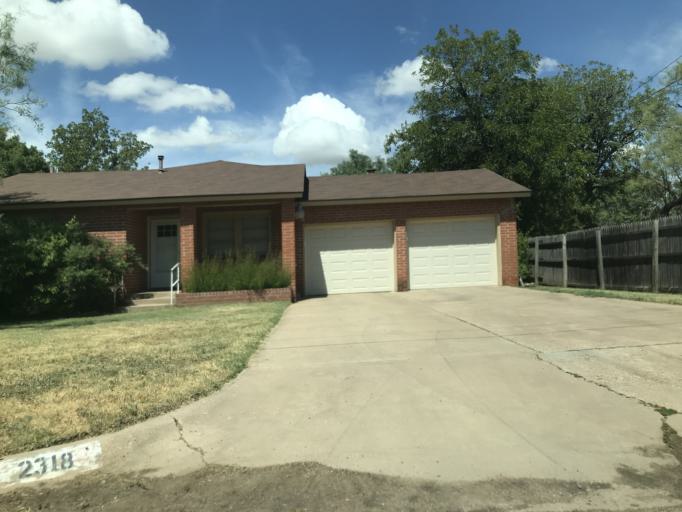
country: US
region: Texas
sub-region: Taylor County
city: Abilene
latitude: 32.4204
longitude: -99.7542
